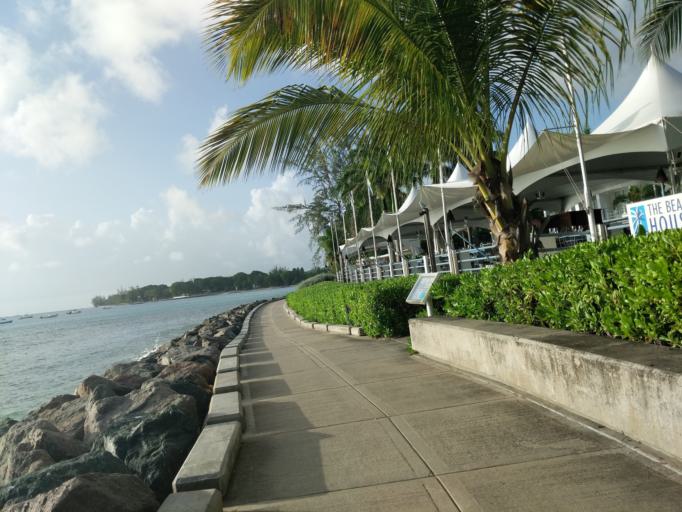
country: BB
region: Saint James
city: Holetown
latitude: 13.1829
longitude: -59.6392
